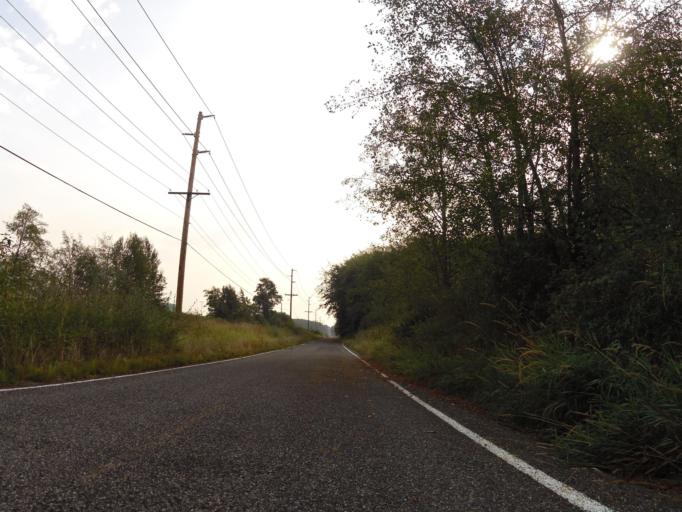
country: US
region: Washington
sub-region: Whatcom County
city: Birch Bay
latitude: 48.8777
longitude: -122.7366
